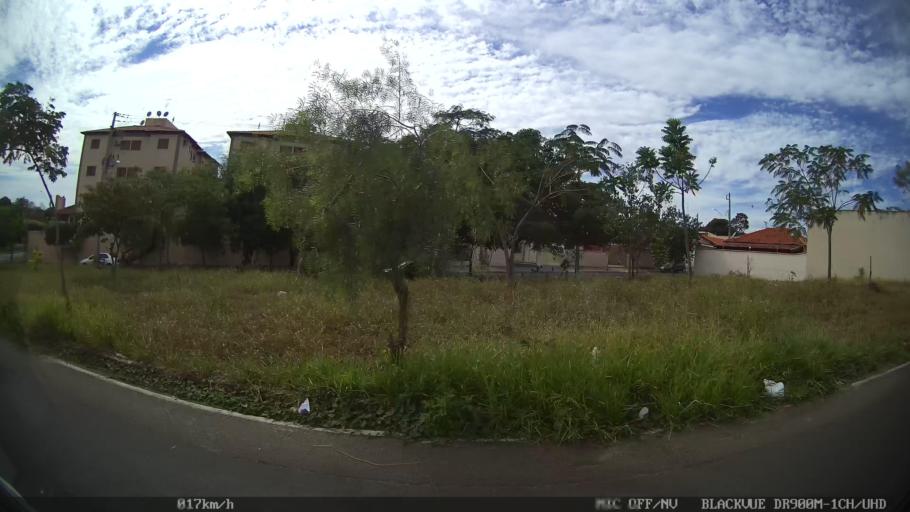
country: BR
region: Sao Paulo
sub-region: Catanduva
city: Catanduva
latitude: -21.1517
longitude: -48.9751
